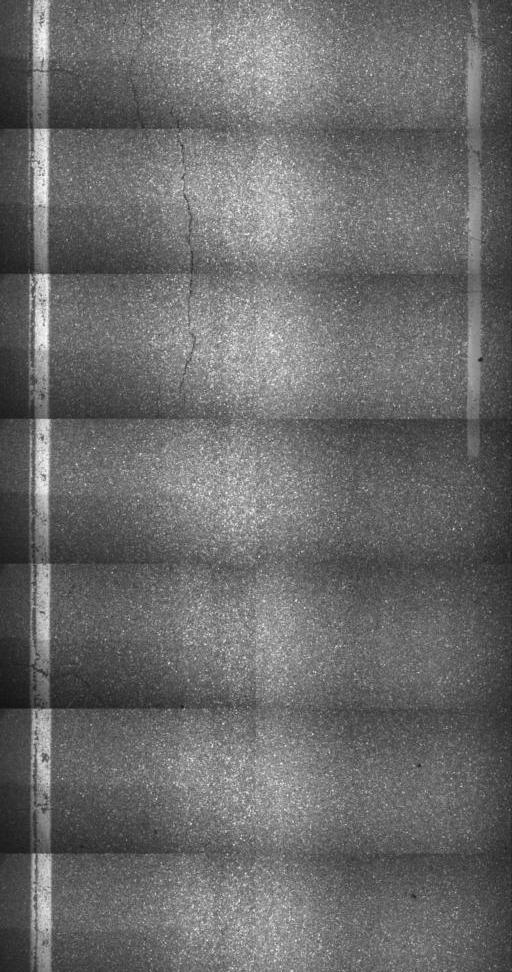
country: US
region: Vermont
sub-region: Addison County
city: Bristol
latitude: 44.1396
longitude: -73.0454
